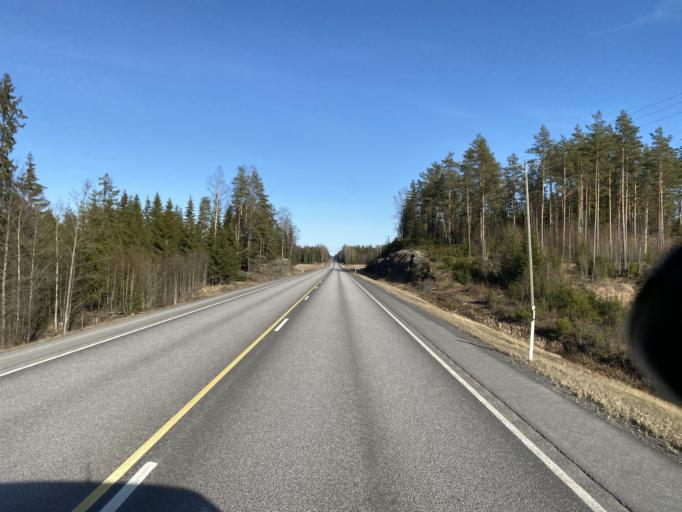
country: FI
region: Satakunta
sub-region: Rauma
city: Eura
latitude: 61.1312
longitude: 22.0385
